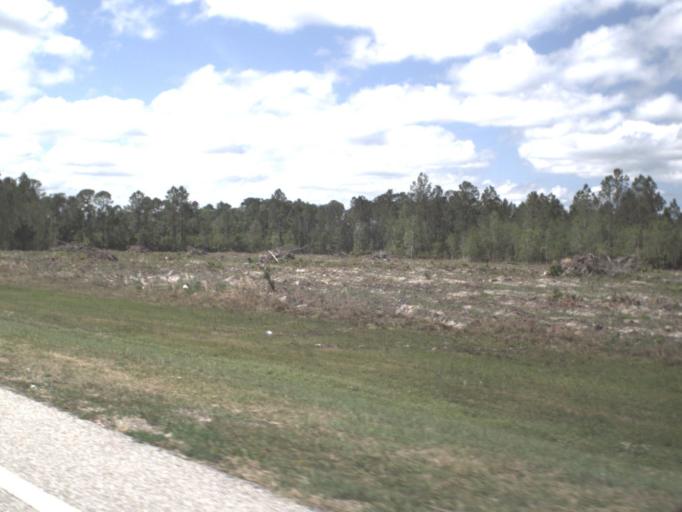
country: US
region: Florida
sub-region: Flagler County
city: Bunnell
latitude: 29.5133
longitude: -81.2640
